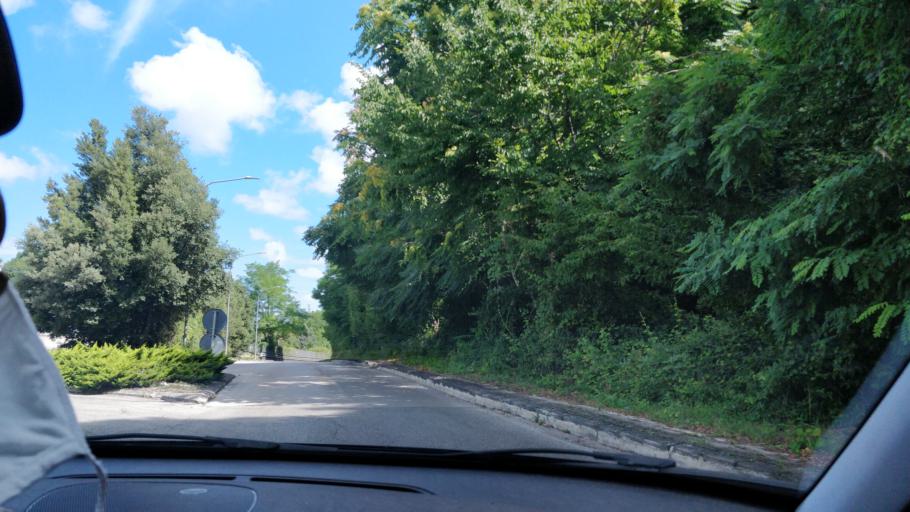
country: IT
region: Abruzzo
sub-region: Provincia di Chieti
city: Lanciano
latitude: 42.2280
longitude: 14.4027
